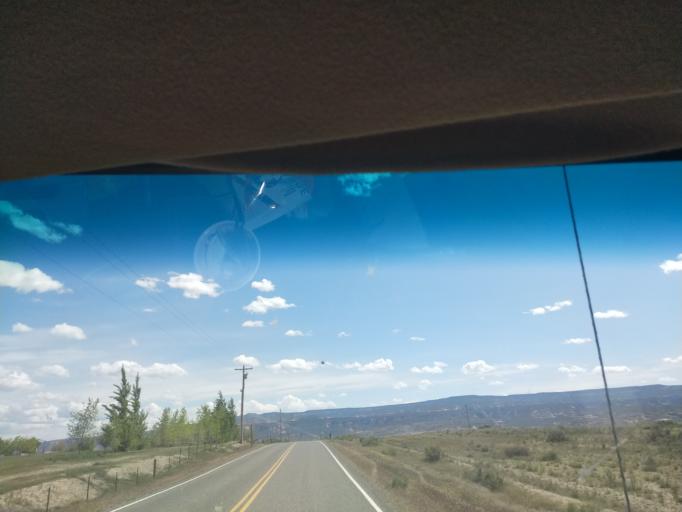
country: US
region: Colorado
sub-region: Mesa County
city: Fruita
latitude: 39.1949
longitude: -108.7571
